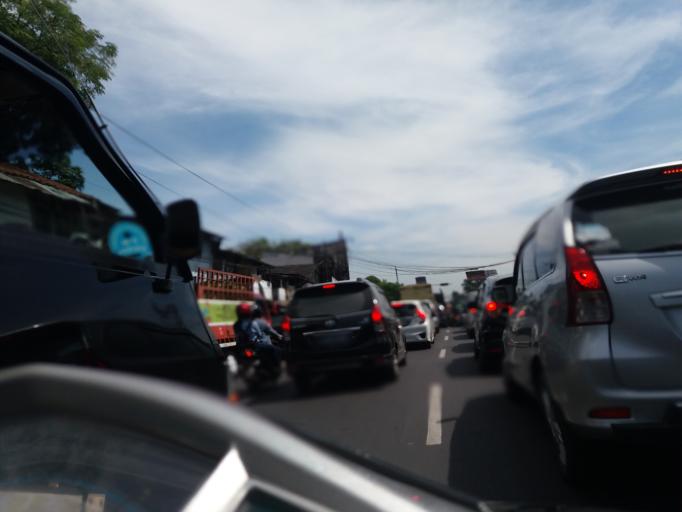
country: ID
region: West Java
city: Bandung
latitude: -6.9484
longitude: 107.6103
